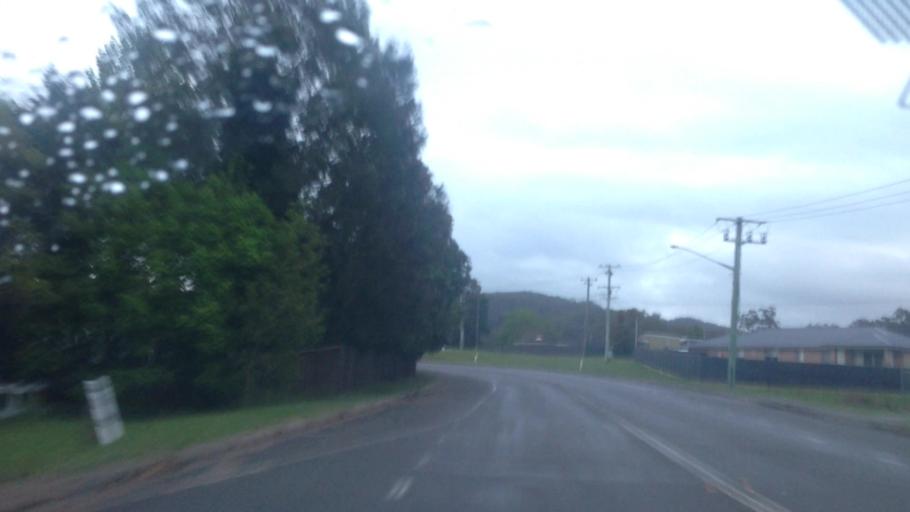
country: AU
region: New South Wales
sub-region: Lake Macquarie Shire
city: Cooranbong
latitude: -33.0796
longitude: 151.4474
